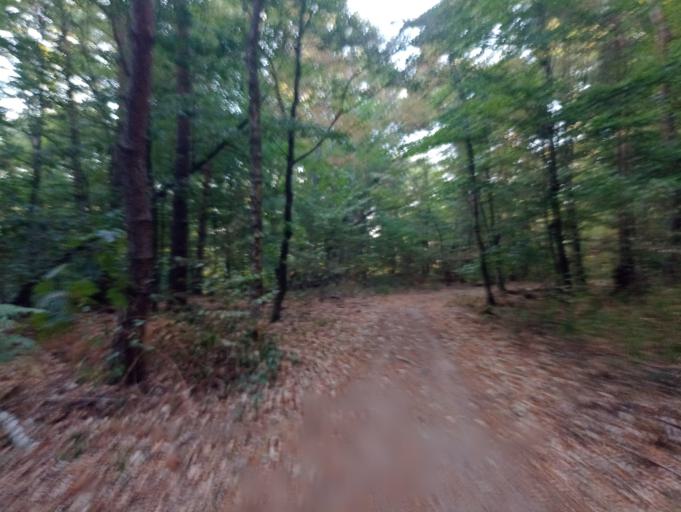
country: DE
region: Hesse
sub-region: Regierungsbezirk Darmstadt
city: Neu Isenburg
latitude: 50.0372
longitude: 8.6499
